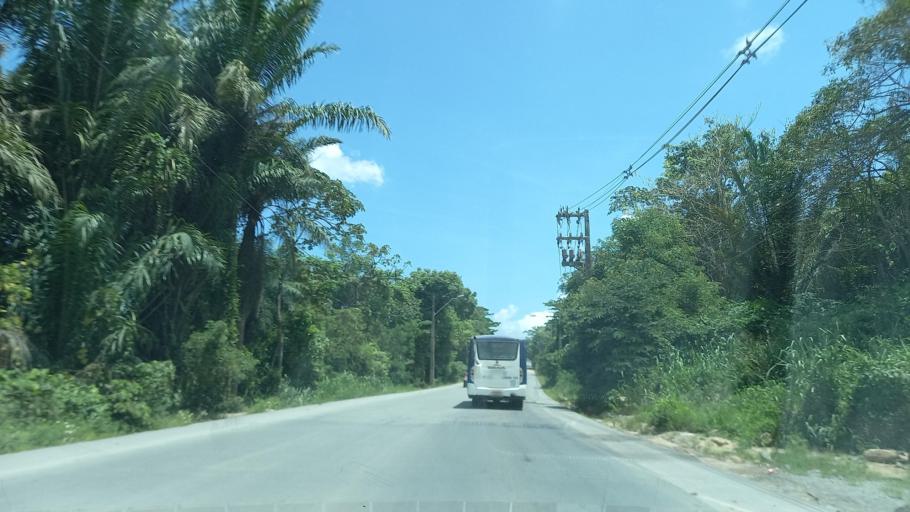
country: BR
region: Pernambuco
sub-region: Jaboatao Dos Guararapes
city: Jaboatao
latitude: -8.1602
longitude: -34.9855
